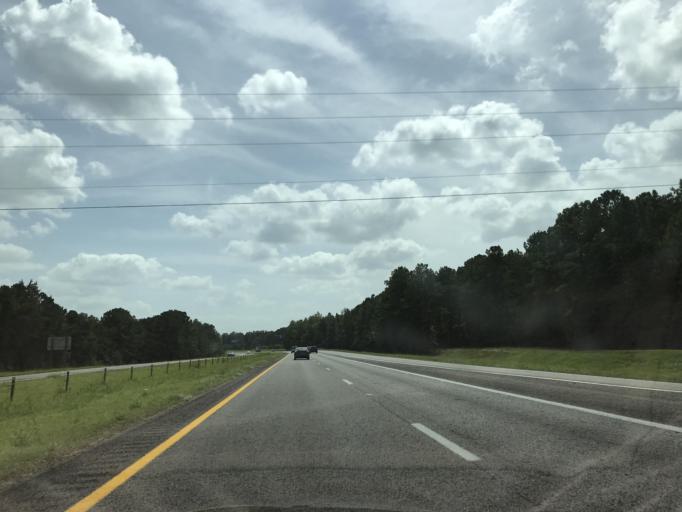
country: US
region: North Carolina
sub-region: Duplin County
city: Wallace
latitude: 34.6852
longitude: -77.9475
